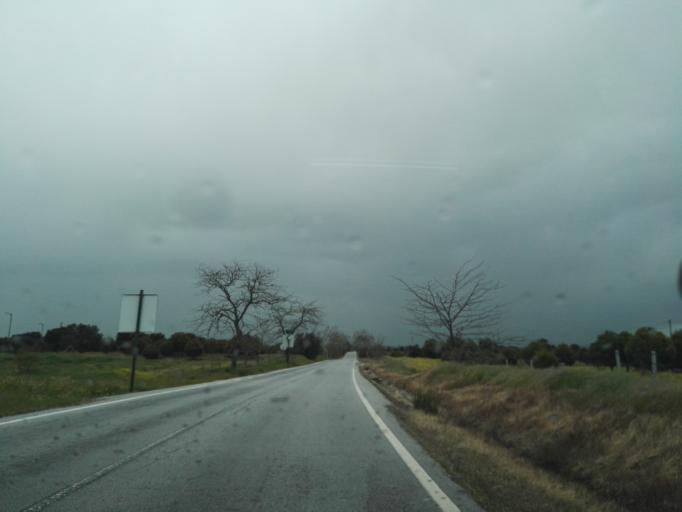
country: PT
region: Portalegre
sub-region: Arronches
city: Arronches
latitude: 39.0159
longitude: -7.2564
